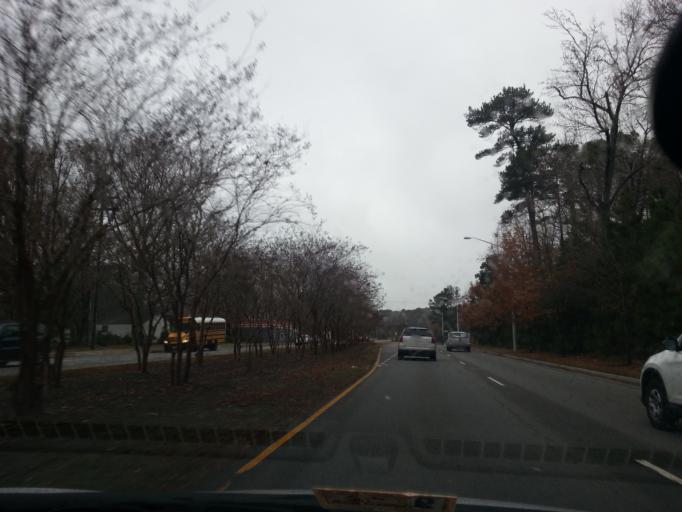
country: US
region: Virginia
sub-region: City of Virginia Beach
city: Virginia Beach
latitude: 36.7975
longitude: -76.0015
